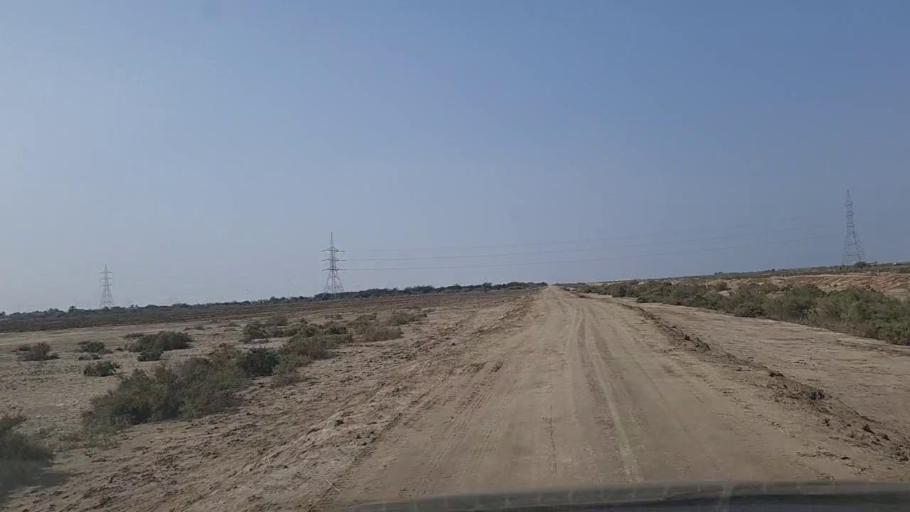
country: PK
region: Sindh
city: Gharo
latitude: 24.7074
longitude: 67.5497
